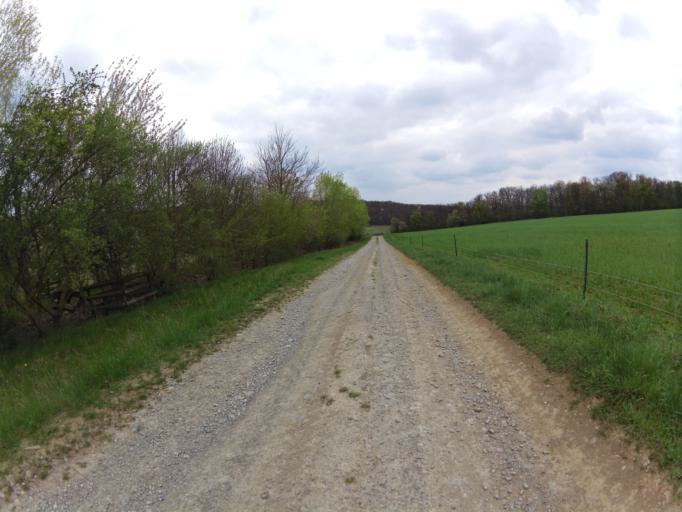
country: DE
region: Bavaria
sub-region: Regierungsbezirk Unterfranken
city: Greussenheim
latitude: 49.8275
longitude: 9.7866
